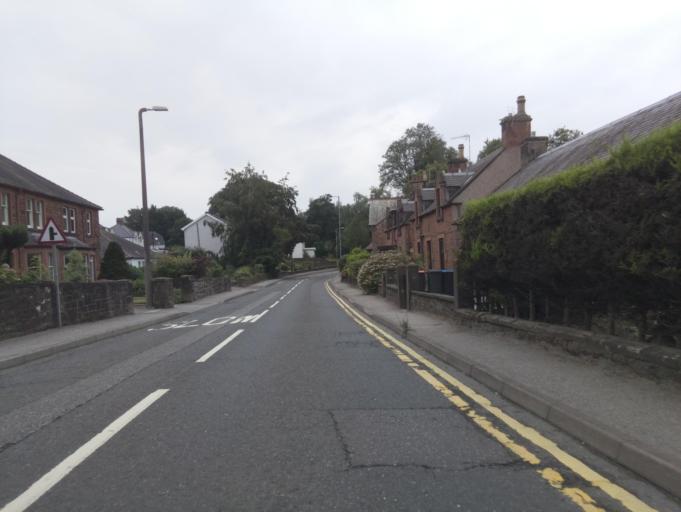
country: GB
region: Scotland
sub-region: Dumfries and Galloway
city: Dumfries
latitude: 55.0770
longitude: -3.5983
